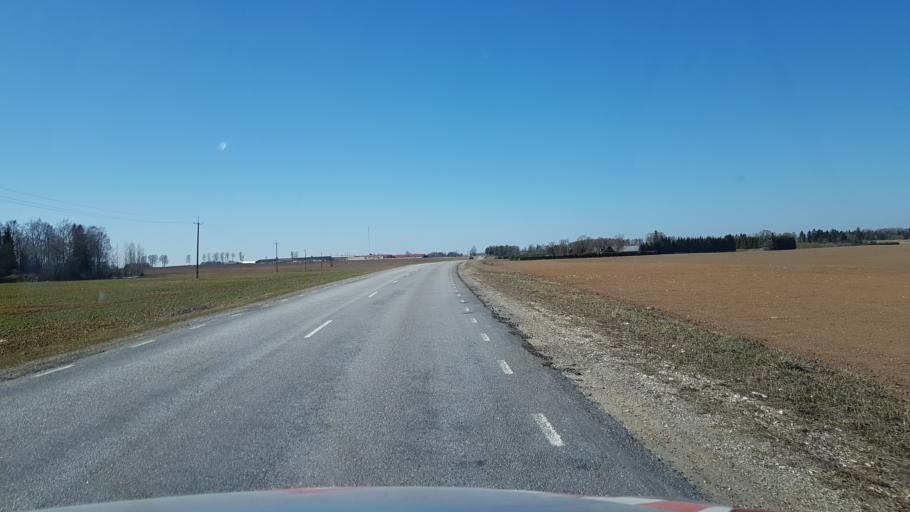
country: EE
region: Laeaene-Virumaa
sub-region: Vaeike-Maarja vald
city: Vaike-Maarja
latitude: 59.1593
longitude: 26.1966
